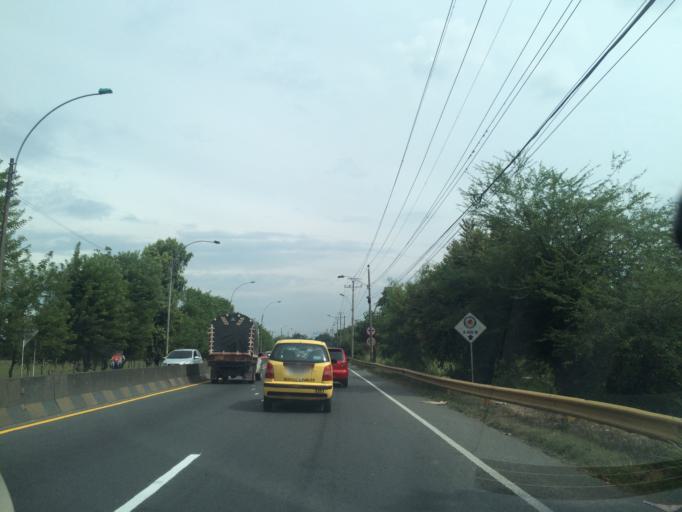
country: CO
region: Valle del Cauca
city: Cali
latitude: 3.3510
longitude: -76.5236
